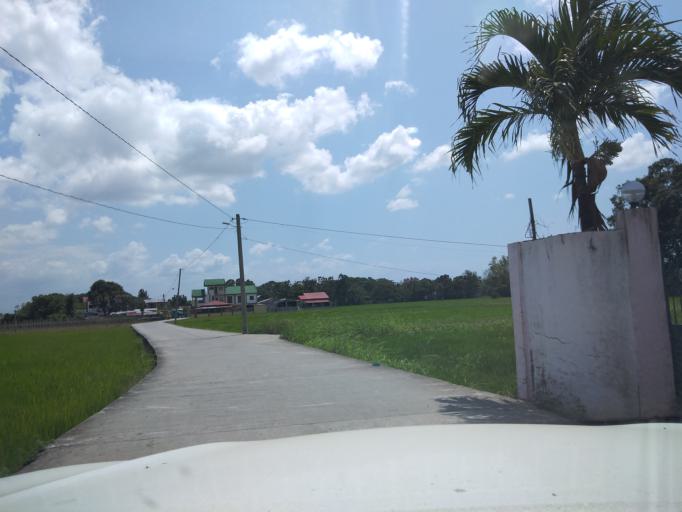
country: PH
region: Central Luzon
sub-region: Province of Pampanga
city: Bahay Pare
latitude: 15.0130
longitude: 120.8718
